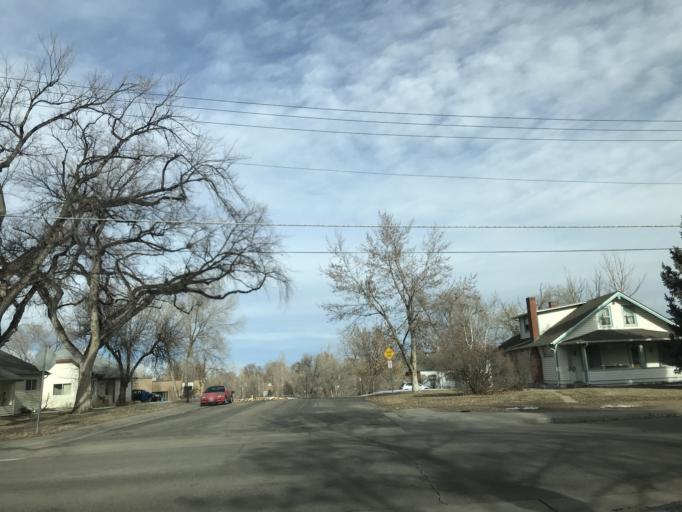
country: US
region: Colorado
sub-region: Arapahoe County
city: Littleton
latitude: 39.6150
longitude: -105.0091
